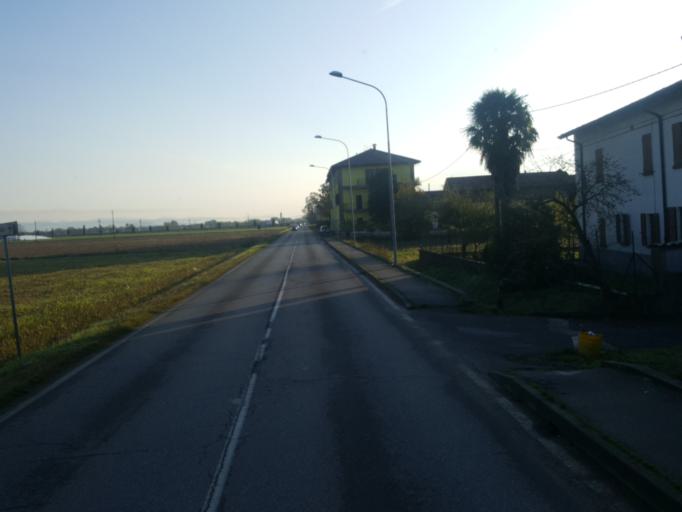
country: IT
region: Lombardy
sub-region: Provincia di Bergamo
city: Pagazzano
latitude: 45.5326
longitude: 9.6803
